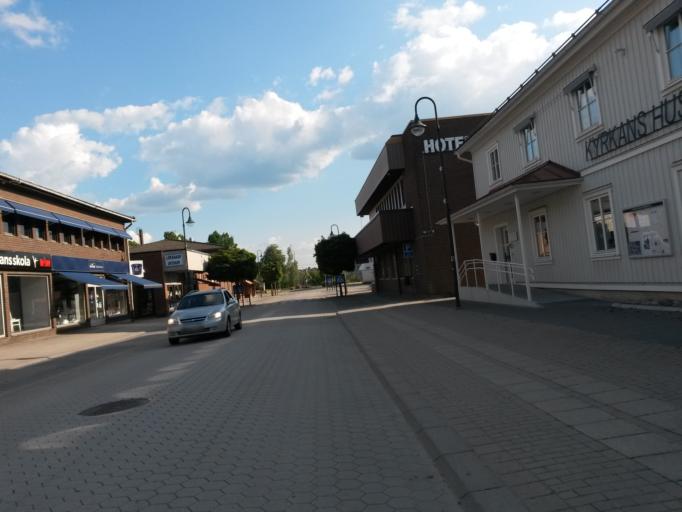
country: SE
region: Vaestra Goetaland
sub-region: Vargarda Kommun
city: Vargarda
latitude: 58.0328
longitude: 12.8086
